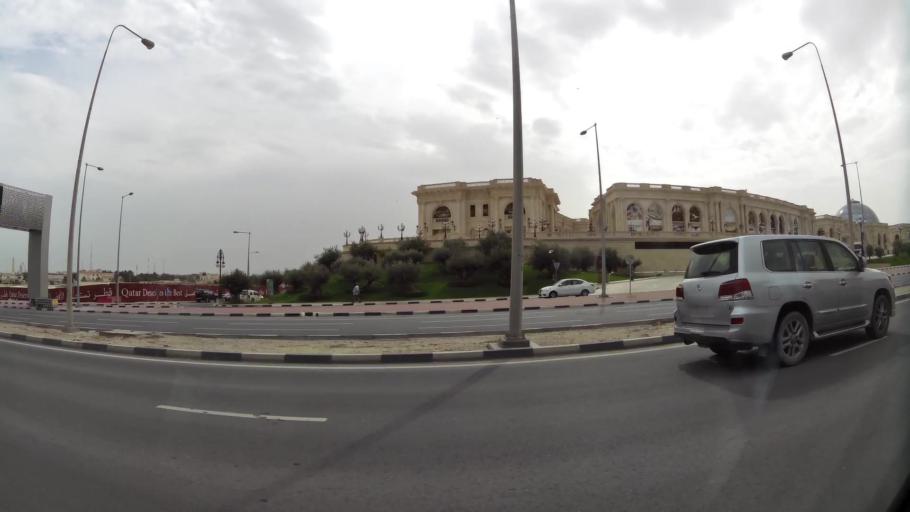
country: QA
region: Baladiyat ad Dawhah
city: Doha
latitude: 25.3321
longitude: 51.4997
